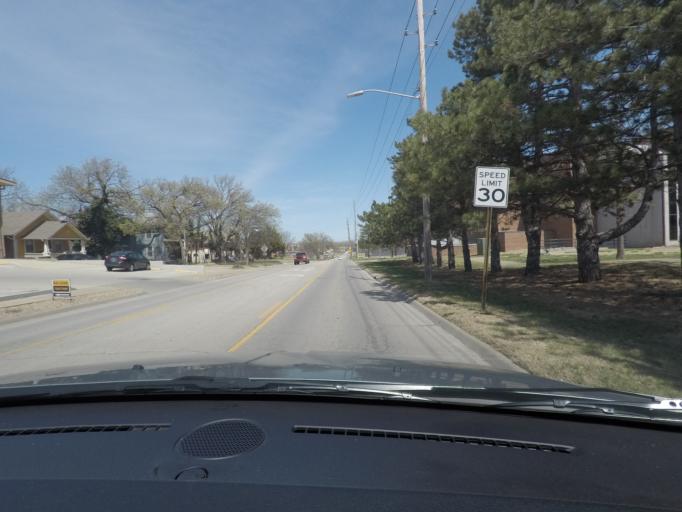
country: US
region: Kansas
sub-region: Lyon County
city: Emporia
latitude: 38.4173
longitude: -96.1818
